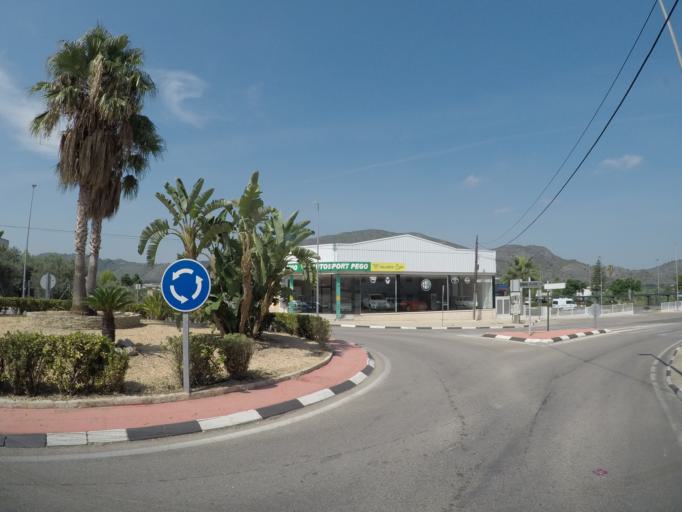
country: ES
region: Valencia
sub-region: Provincia de Alicante
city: Pego
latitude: 38.8480
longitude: -0.1142
